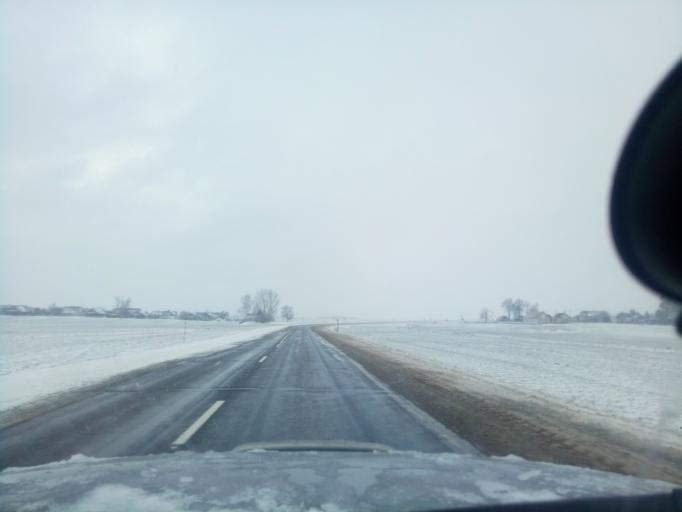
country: BY
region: Minsk
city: Haradzyeya
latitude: 53.3035
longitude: 26.5737
